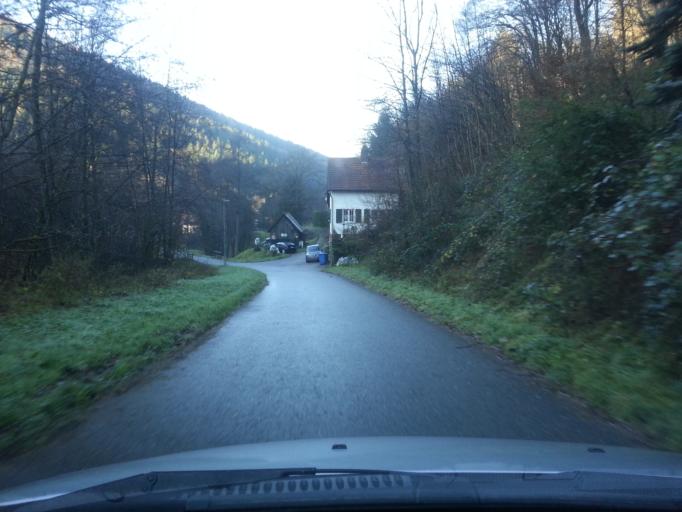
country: DE
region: Baden-Wuerttemberg
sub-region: Karlsruhe Region
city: Zwingenberg
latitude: 49.4827
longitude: 9.0661
